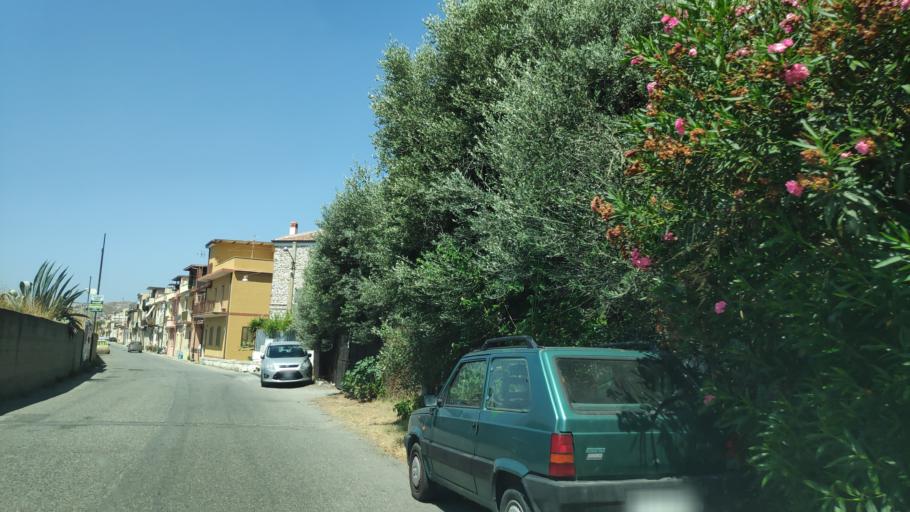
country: IT
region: Calabria
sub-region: Provincia di Reggio Calabria
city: Bova Marina
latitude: 37.9292
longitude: 15.9312
